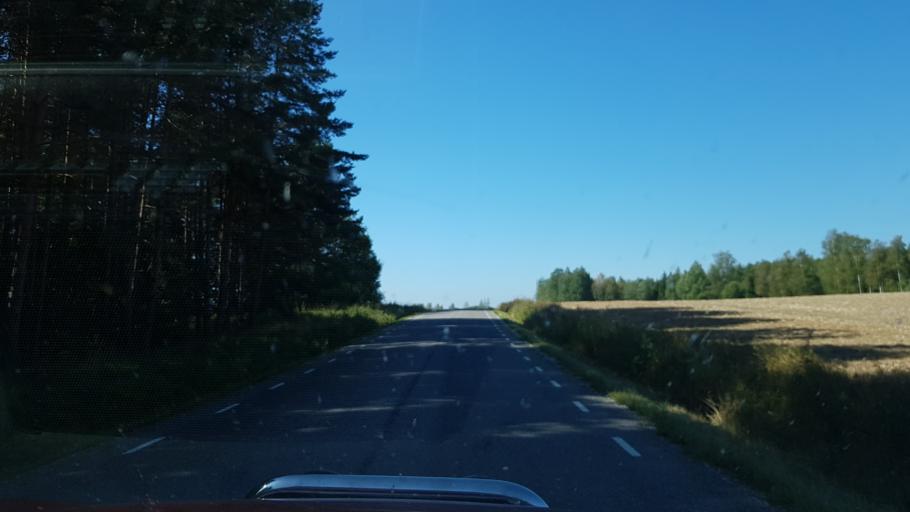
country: EE
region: Polvamaa
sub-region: Polva linn
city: Polva
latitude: 58.2098
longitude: 27.1311
